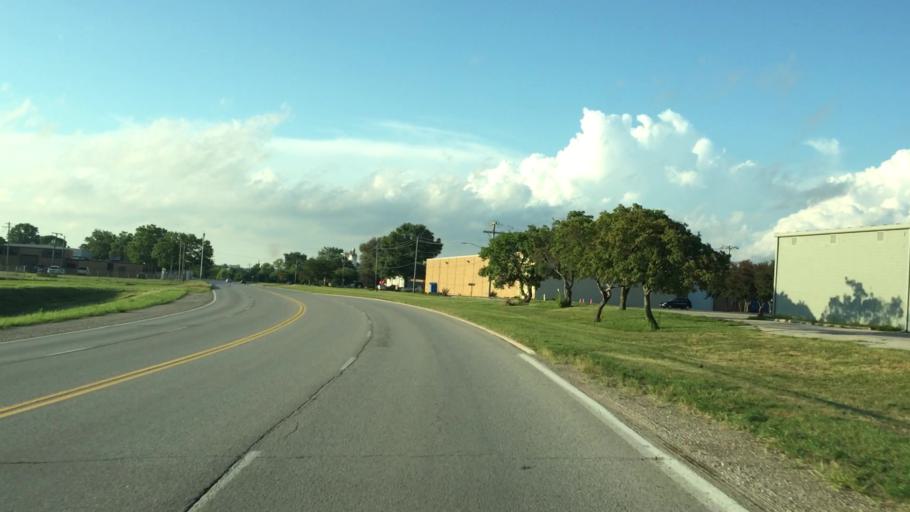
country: US
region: Iowa
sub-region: Johnson County
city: University Heights
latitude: 41.6347
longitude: -91.5386
